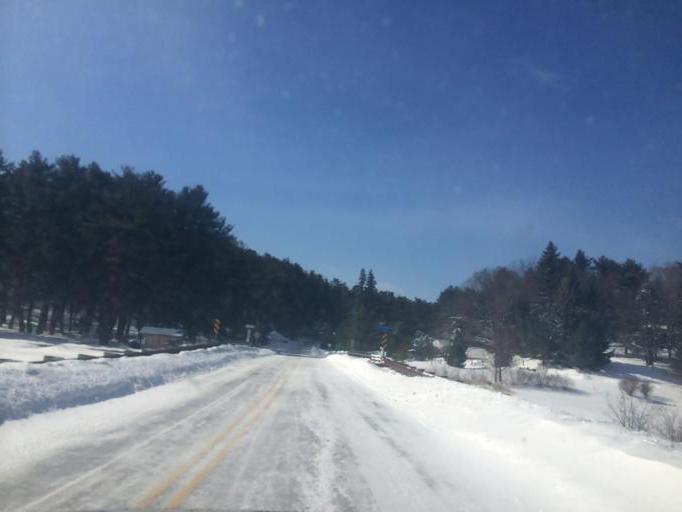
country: US
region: Pennsylvania
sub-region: Centre County
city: Stormstown
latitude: 40.9152
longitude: -78.0594
